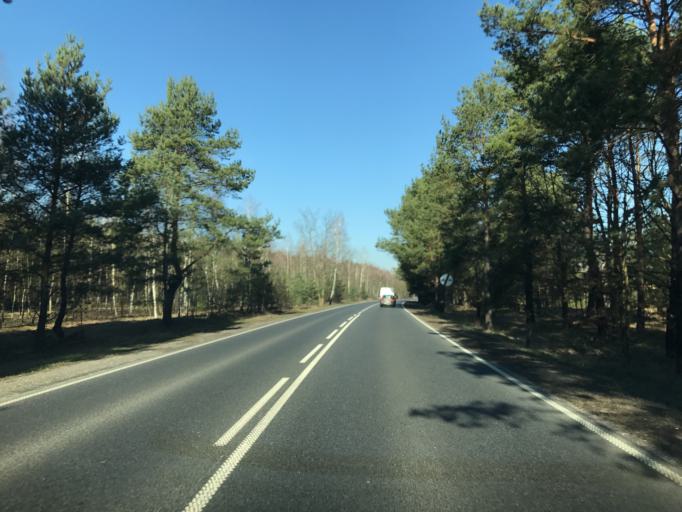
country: PL
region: Kujawsko-Pomorskie
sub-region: Bydgoszcz
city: Fordon
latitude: 53.0781
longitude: 18.1276
